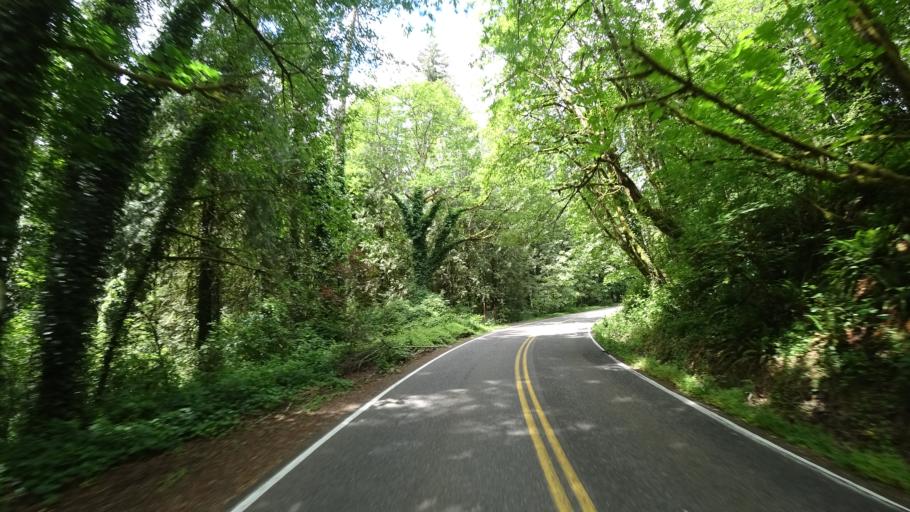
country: US
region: Oregon
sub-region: Clackamas County
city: Lake Oswego
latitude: 45.4454
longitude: -122.6913
